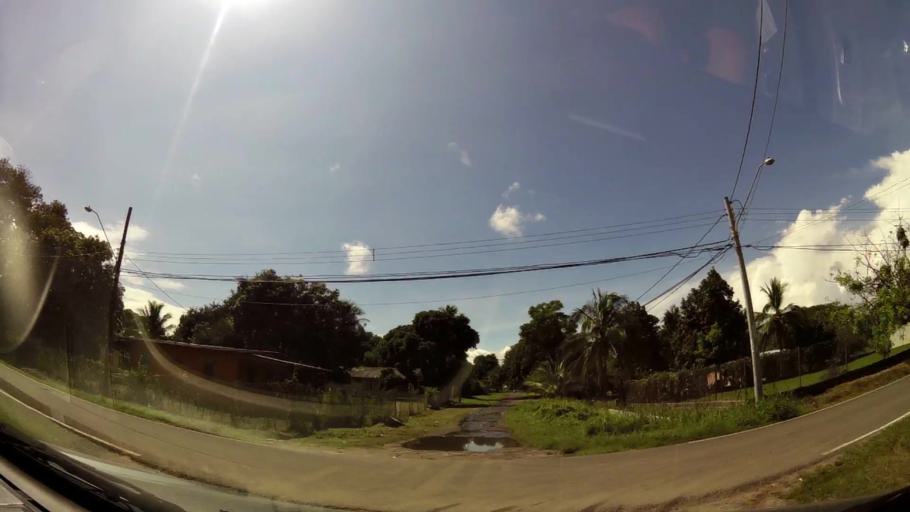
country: PA
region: Panama
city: Nueva Gorgona
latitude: 8.5564
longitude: -79.8730
